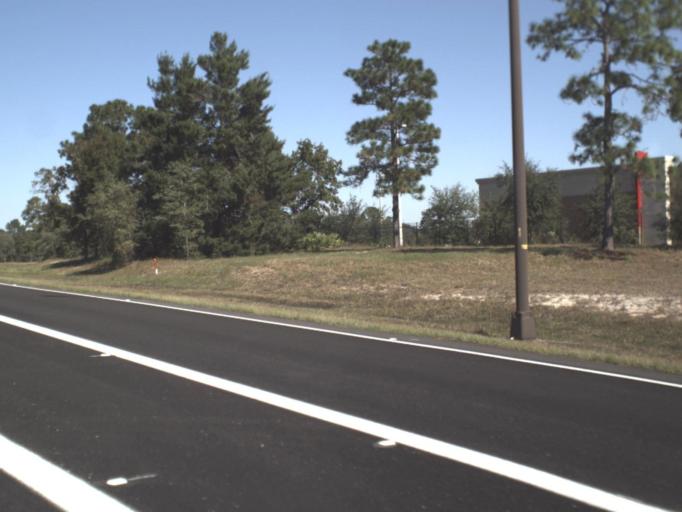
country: US
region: Florida
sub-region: Hernando County
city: Masaryktown
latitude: 28.4783
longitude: -82.4807
